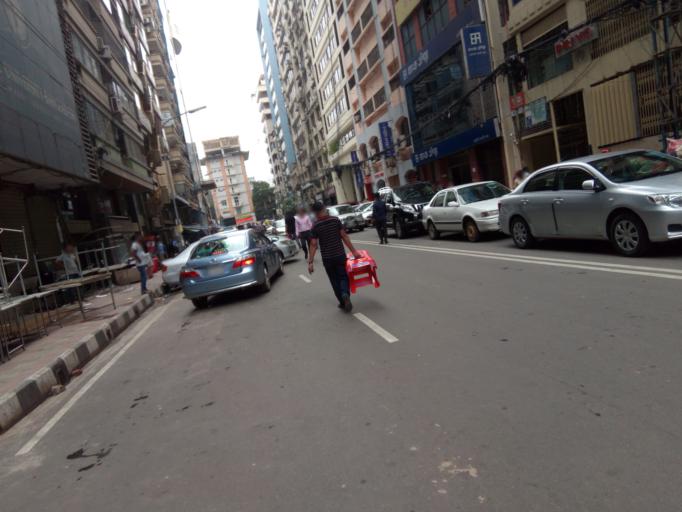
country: BD
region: Dhaka
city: Paltan
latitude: 23.7935
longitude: 90.4045
